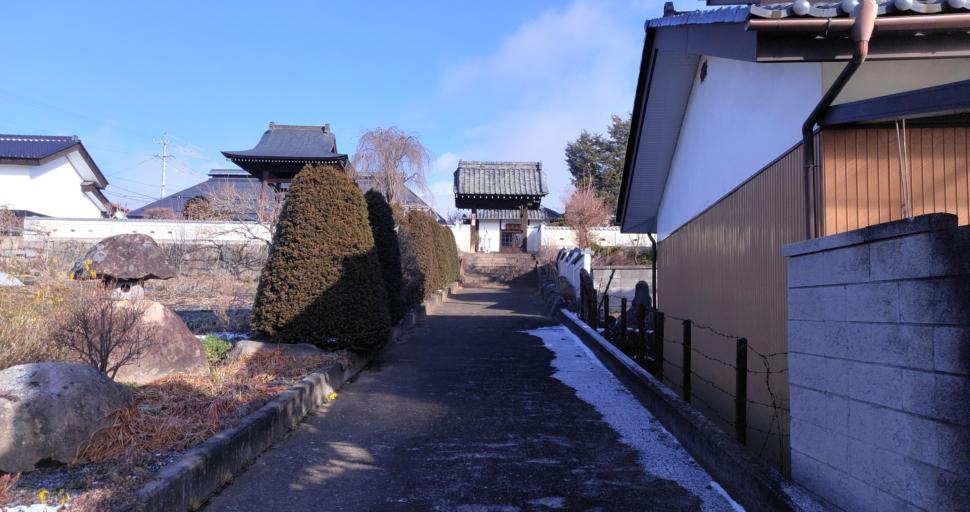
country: JP
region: Nagano
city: Komoro
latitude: 36.3653
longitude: 138.3698
